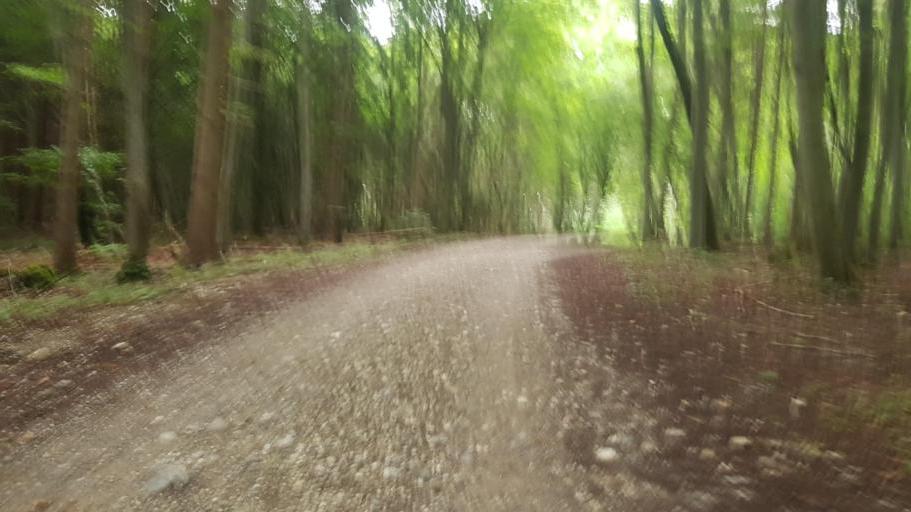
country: DE
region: Bavaria
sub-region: Upper Bavaria
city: Starnberg
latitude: 48.0328
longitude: 11.3540
